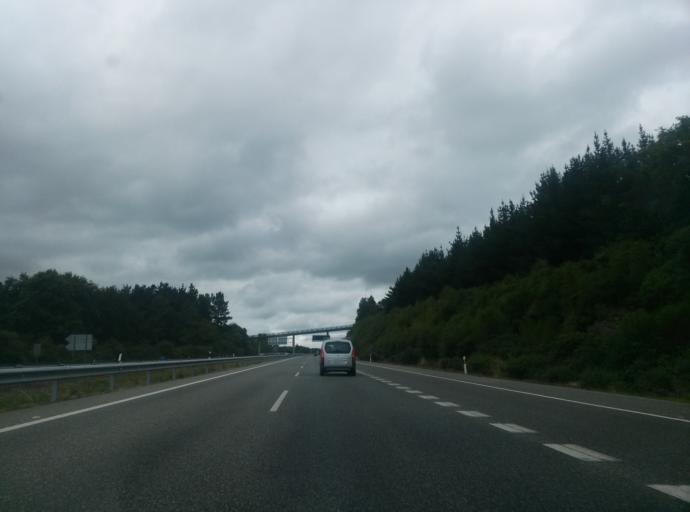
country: ES
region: Galicia
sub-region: Provincia de Lugo
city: Vilalba
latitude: 43.3052
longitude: -7.7037
